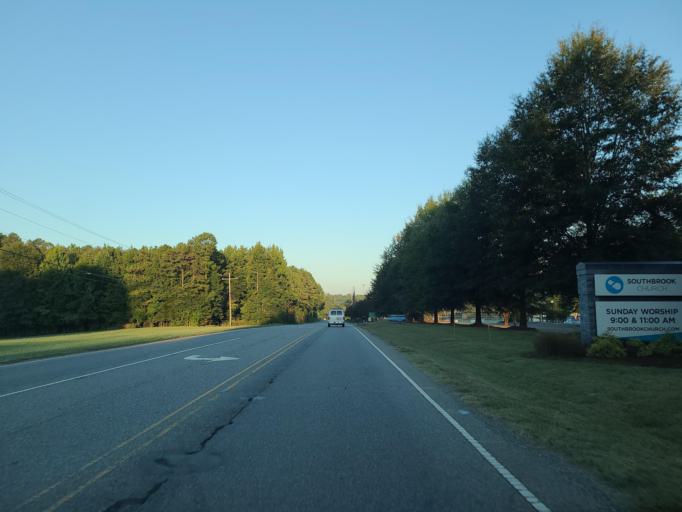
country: US
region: North Carolina
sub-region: Union County
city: Wesley Chapel
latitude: 35.0010
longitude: -80.7087
